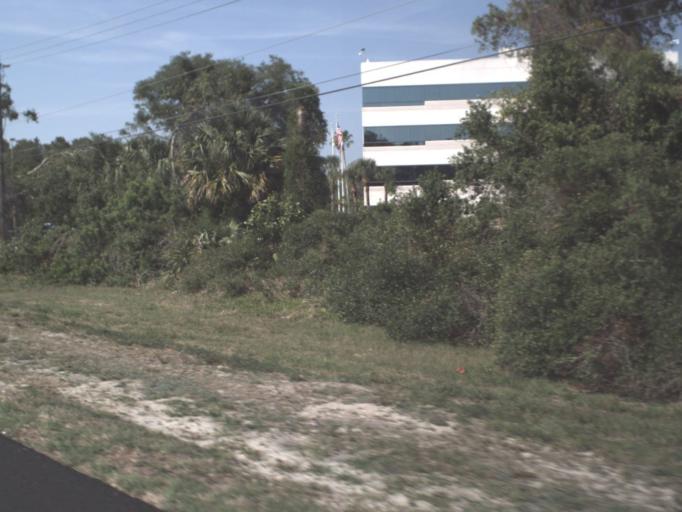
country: US
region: Florida
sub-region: Brevard County
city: Port Saint John
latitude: 28.5189
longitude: -80.7865
